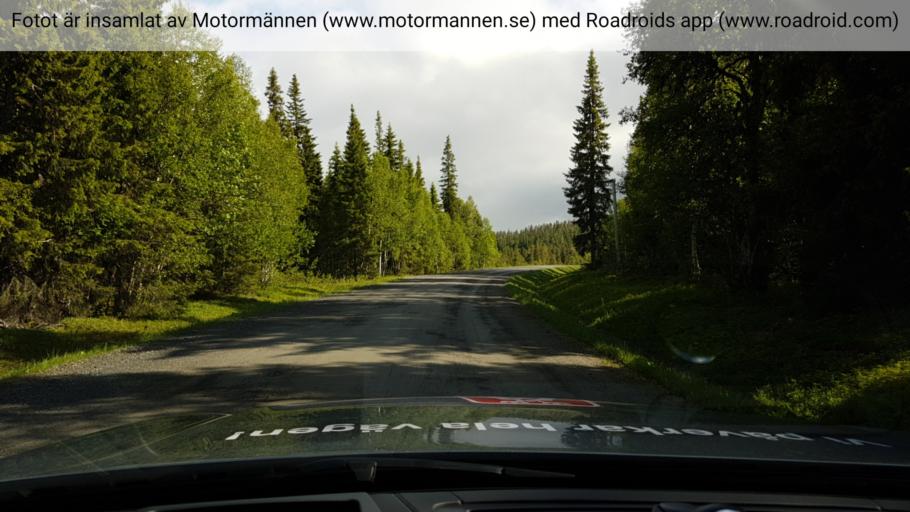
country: NO
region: Nord-Trondelag
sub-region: Snasa
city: Snaase
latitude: 63.7272
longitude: 12.4761
